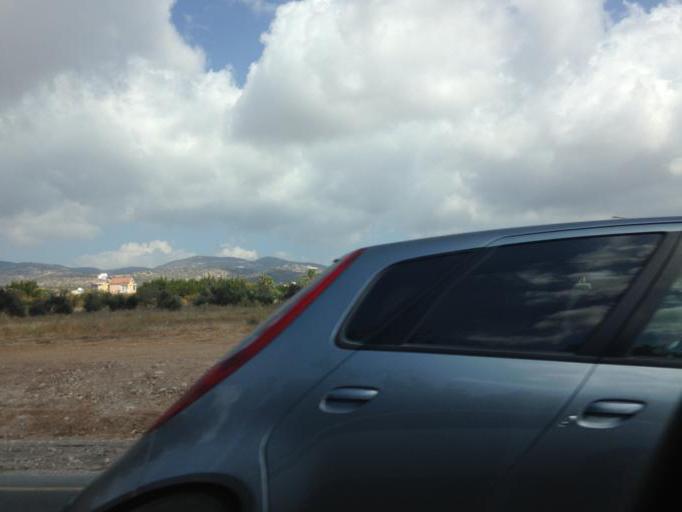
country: CY
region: Pafos
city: Pegeia
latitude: 34.8583
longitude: 32.3799
